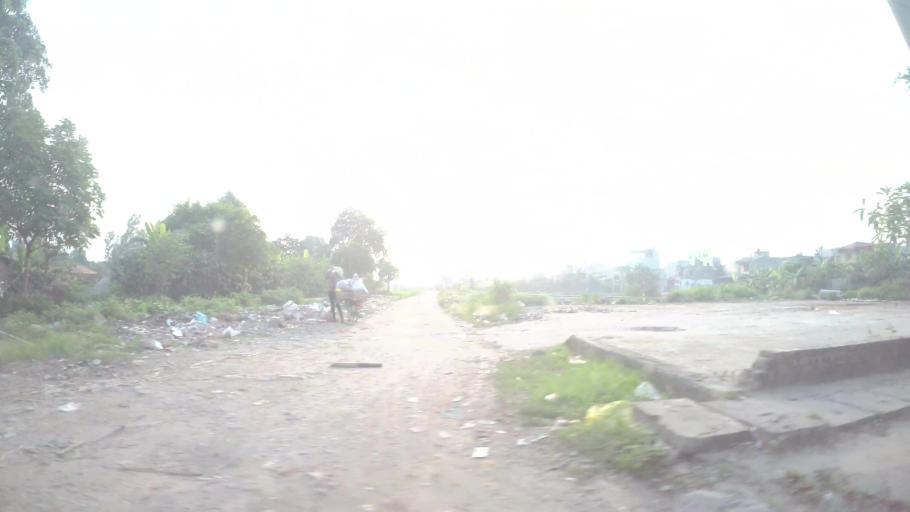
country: VN
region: Ha Noi
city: Van Dien
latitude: 20.9296
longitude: 105.8355
